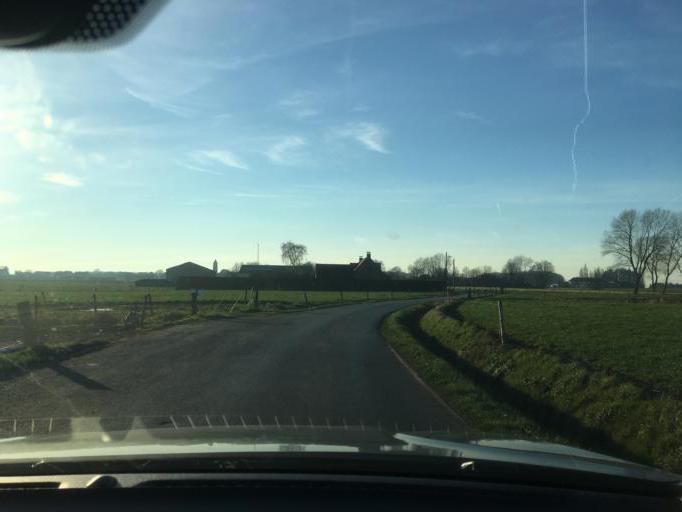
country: BE
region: Flanders
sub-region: Provincie West-Vlaanderen
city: Pittem
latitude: 50.9647
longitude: 3.2526
